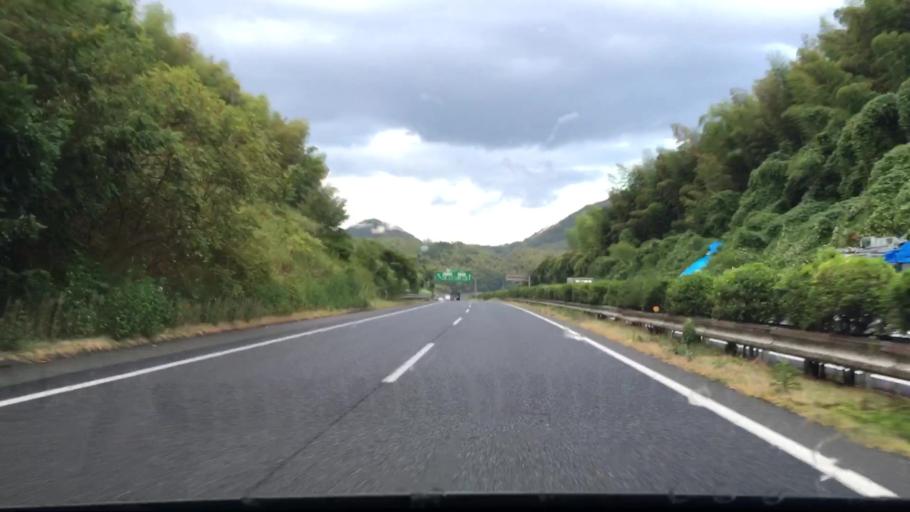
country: JP
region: Fukuoka
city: Kitakyushu
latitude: 33.8035
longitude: 130.8724
